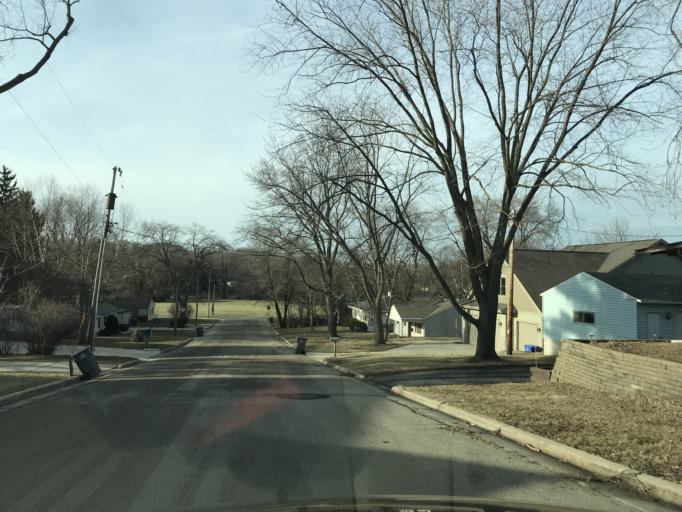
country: US
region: Wisconsin
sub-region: Dane County
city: Monona
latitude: 43.0603
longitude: -89.3422
